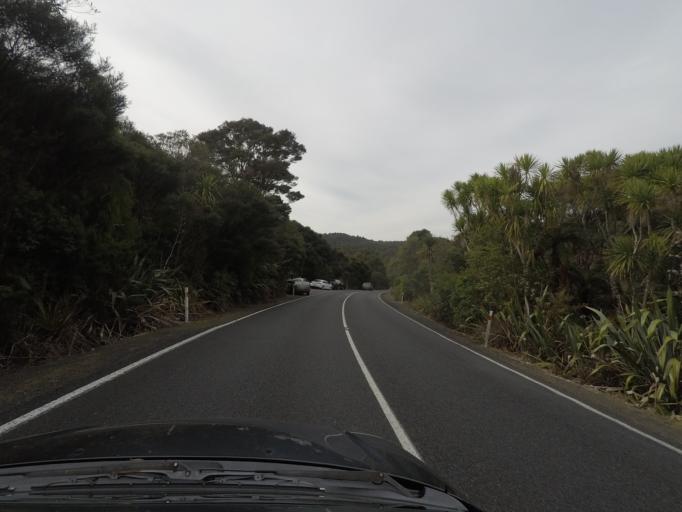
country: NZ
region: Auckland
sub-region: Auckland
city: Titirangi
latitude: -36.9370
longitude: 174.5561
